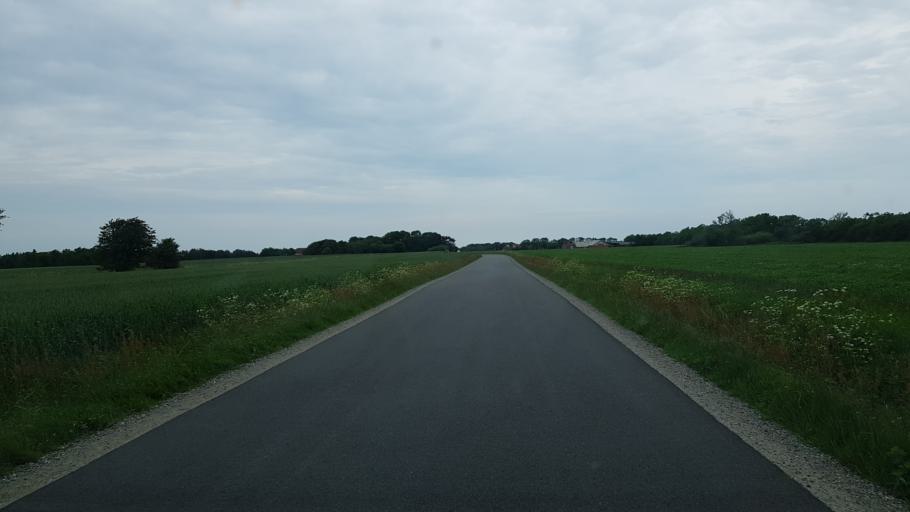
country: DK
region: South Denmark
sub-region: Varde Kommune
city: Oksbol
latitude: 55.7185
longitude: 8.3688
